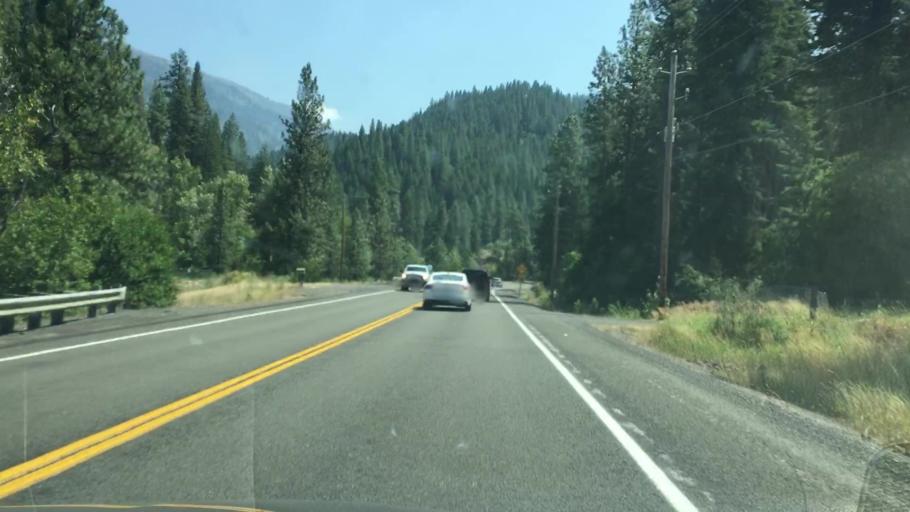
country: US
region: Idaho
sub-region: Valley County
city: McCall
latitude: 45.1871
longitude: -116.3040
